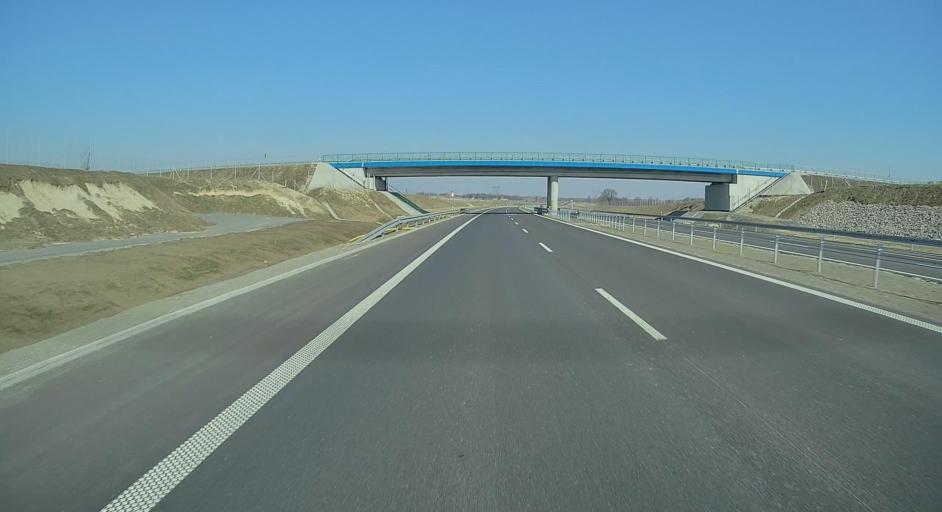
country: PL
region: Lublin Voivodeship
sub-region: Powiat janowski
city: Modliborzyce
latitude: 50.7911
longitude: 22.2923
